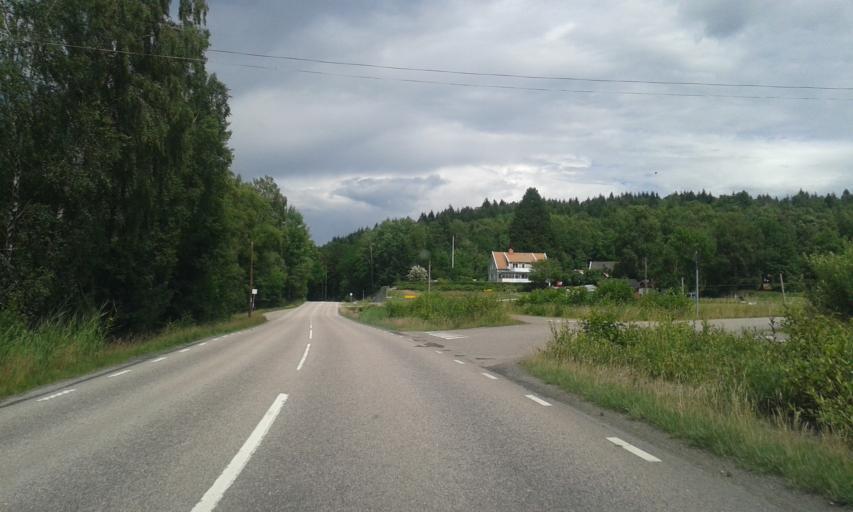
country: SE
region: Vaestra Goetaland
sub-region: Kungalvs Kommun
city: Diserod
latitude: 57.8944
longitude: 12.0025
